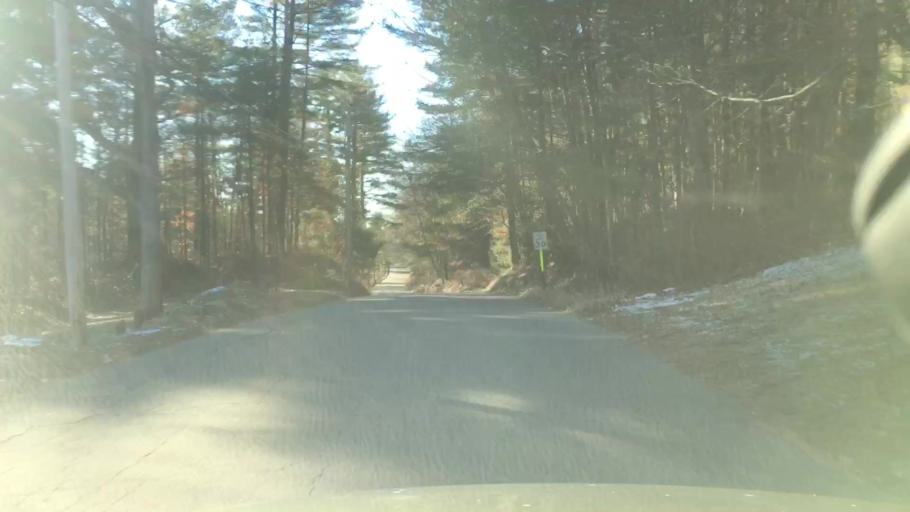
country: US
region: Connecticut
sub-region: Tolland County
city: Stafford
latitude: 41.9731
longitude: -72.2975
